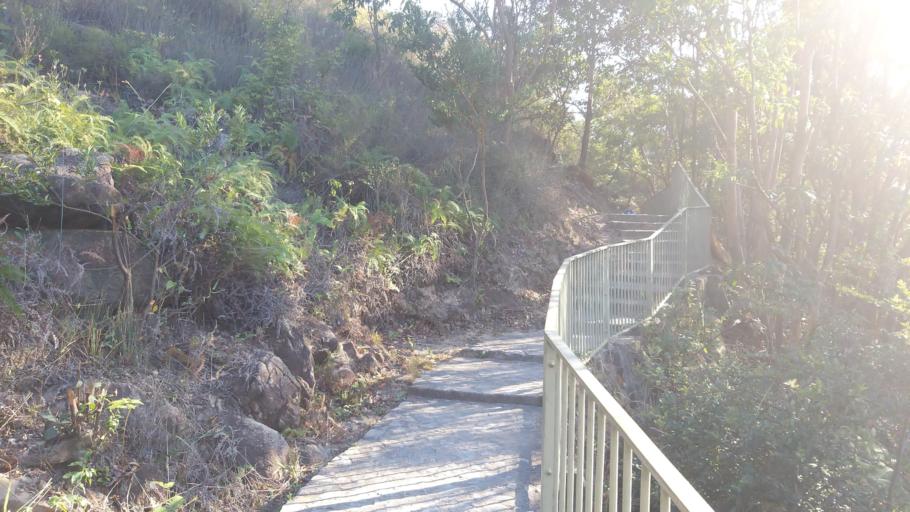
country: HK
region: Tuen Mun
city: Tuen Mun
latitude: 22.3982
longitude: 113.9836
